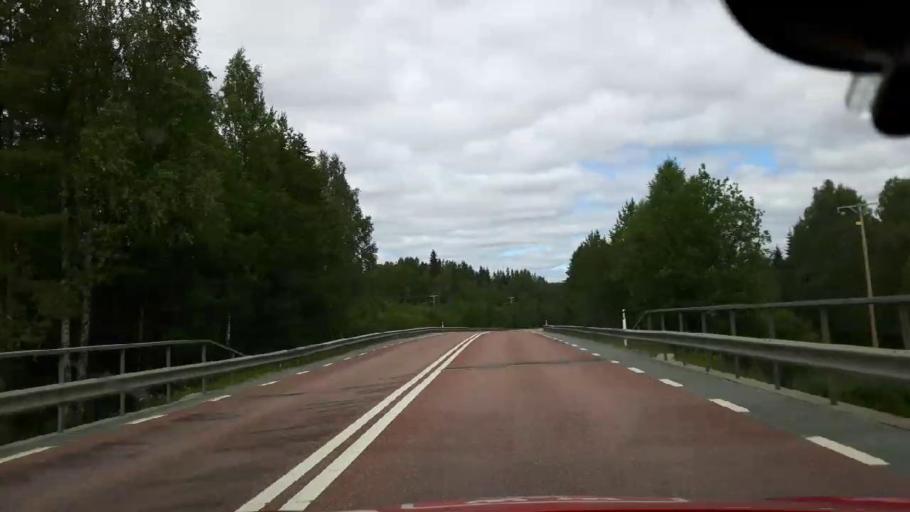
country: SE
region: Jaemtland
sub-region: Braecke Kommun
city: Braecke
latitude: 62.7669
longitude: 15.4057
